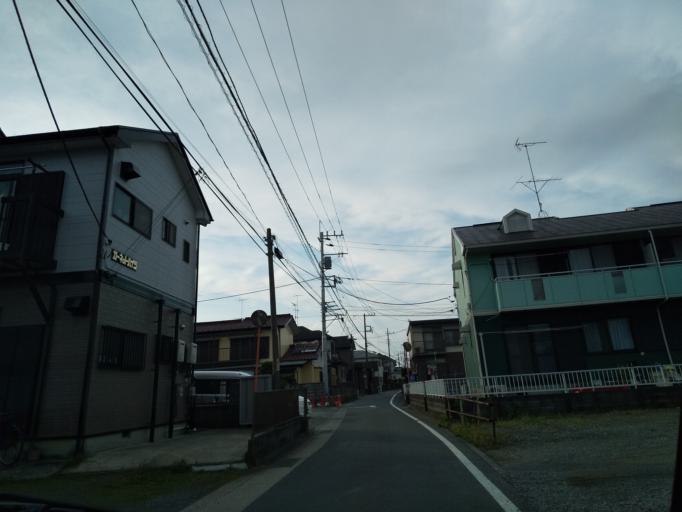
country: JP
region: Kanagawa
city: Zama
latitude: 35.5059
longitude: 139.3620
